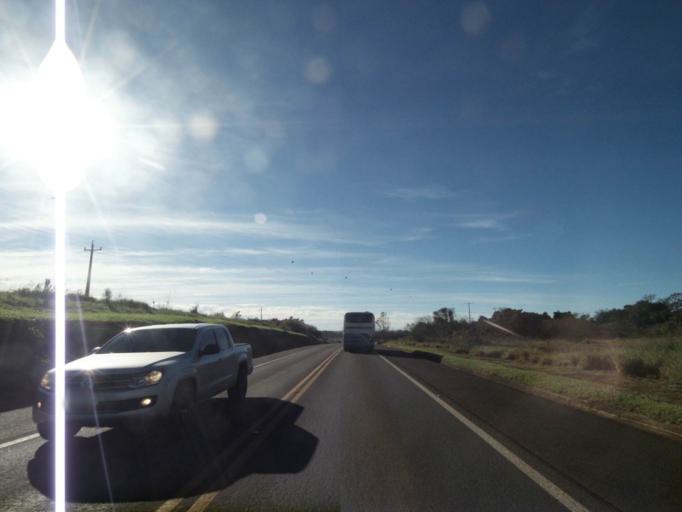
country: BR
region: Parana
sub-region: Cascavel
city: Cascavel
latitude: -25.0292
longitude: -53.5713
